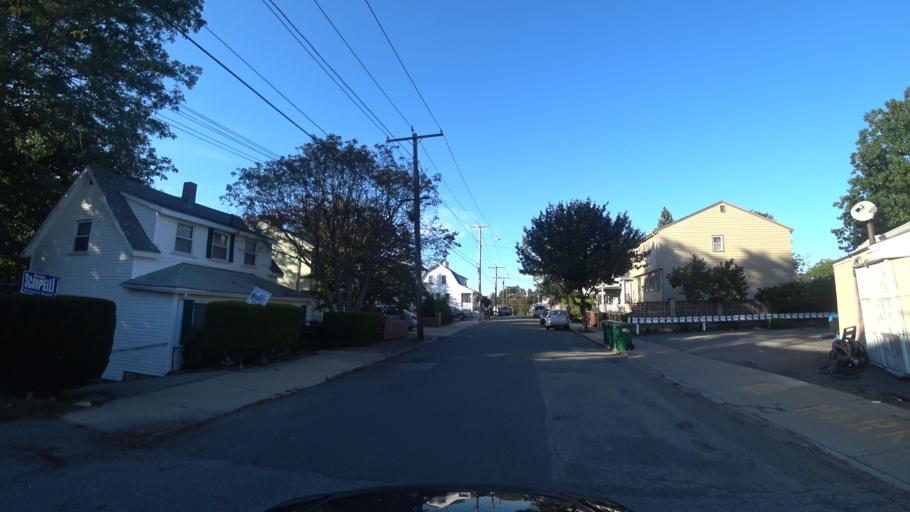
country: US
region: Massachusetts
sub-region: Middlesex County
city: Medford
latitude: 42.4359
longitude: -71.0964
